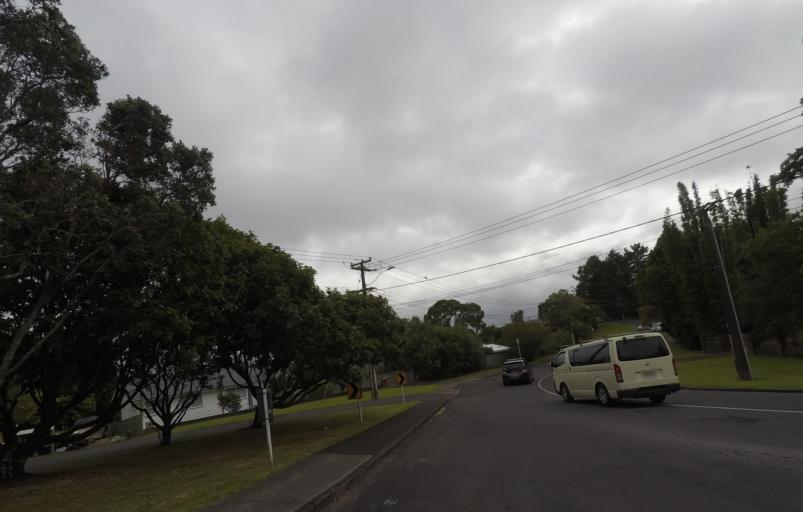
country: NZ
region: Auckland
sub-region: Auckland
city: Titirangi
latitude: -36.9372
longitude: 174.6690
